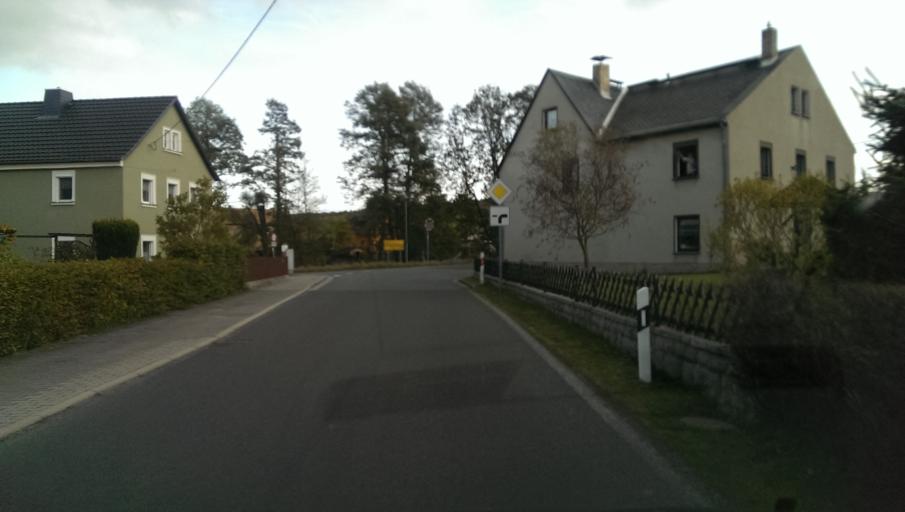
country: DE
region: Saxony
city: Steina
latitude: 51.2135
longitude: 14.0743
